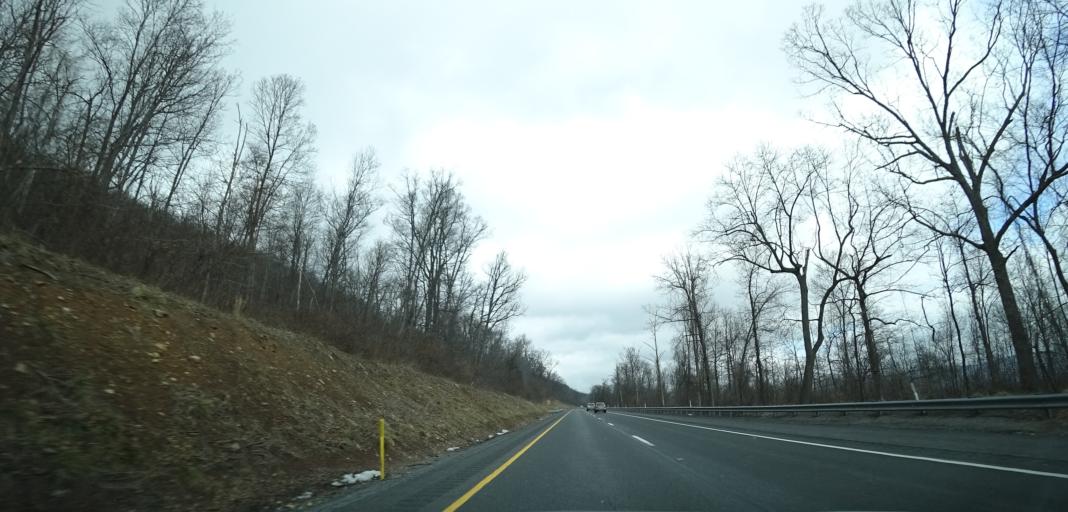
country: US
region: Maryland
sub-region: Washington County
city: Hancock
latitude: 39.8460
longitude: -78.2738
